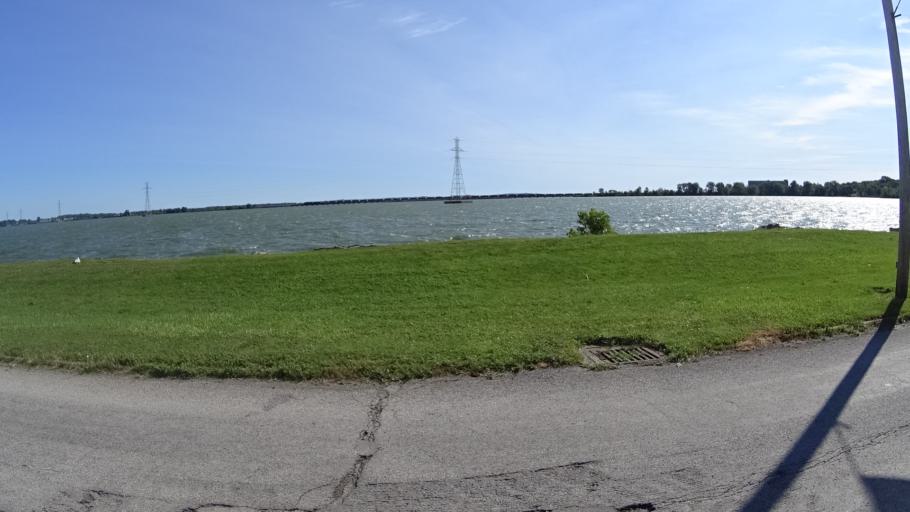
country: US
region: Ohio
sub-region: Erie County
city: Sandusky
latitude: 41.4701
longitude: -82.8224
